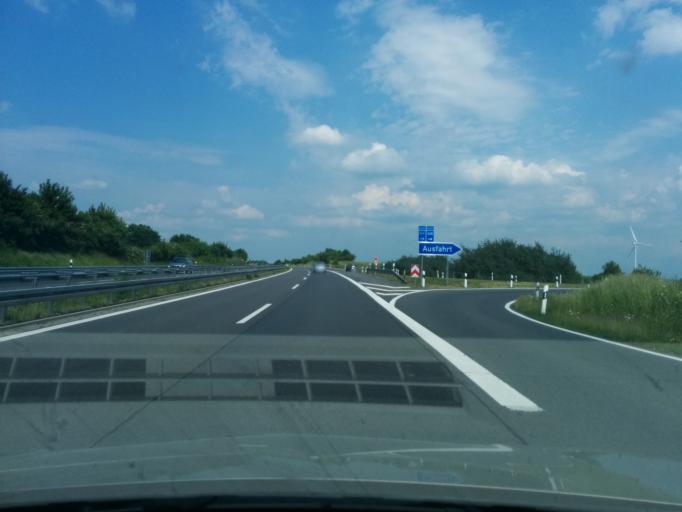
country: DE
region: Brandenburg
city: Grunow
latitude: 53.3072
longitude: 13.9919
